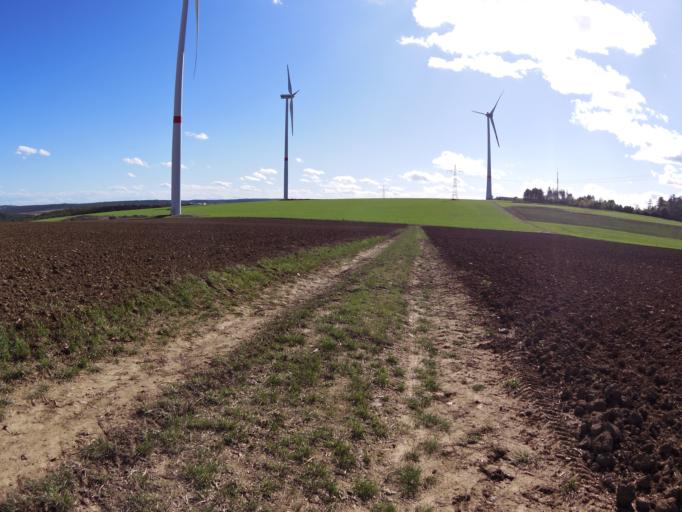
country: DE
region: Bavaria
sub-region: Regierungsbezirk Unterfranken
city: Hettstadt
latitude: 49.8324
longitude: 9.8237
